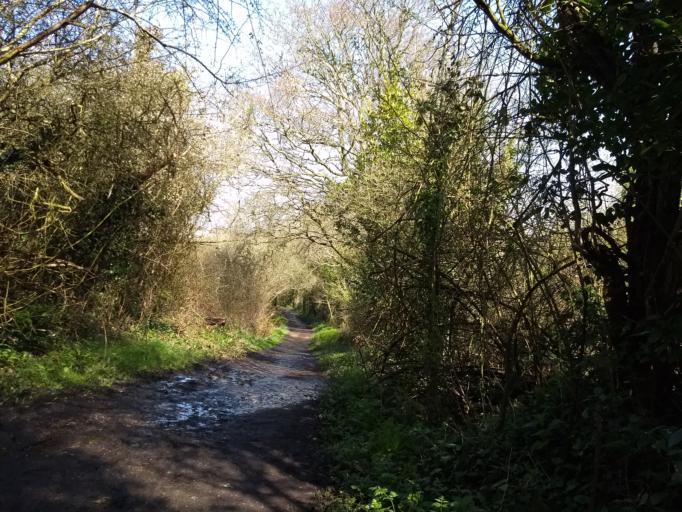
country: GB
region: England
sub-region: Isle of Wight
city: Ryde
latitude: 50.7198
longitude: -1.1628
